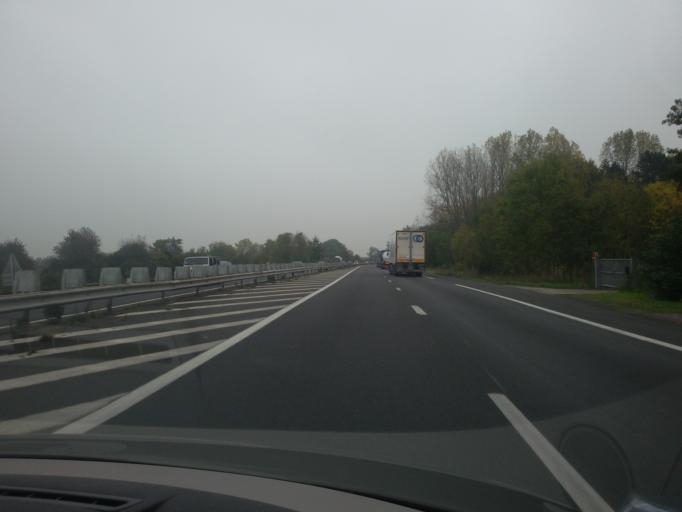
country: FR
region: Lower Normandy
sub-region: Departement du Calvados
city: Touques
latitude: 49.2528
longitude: 0.0752
